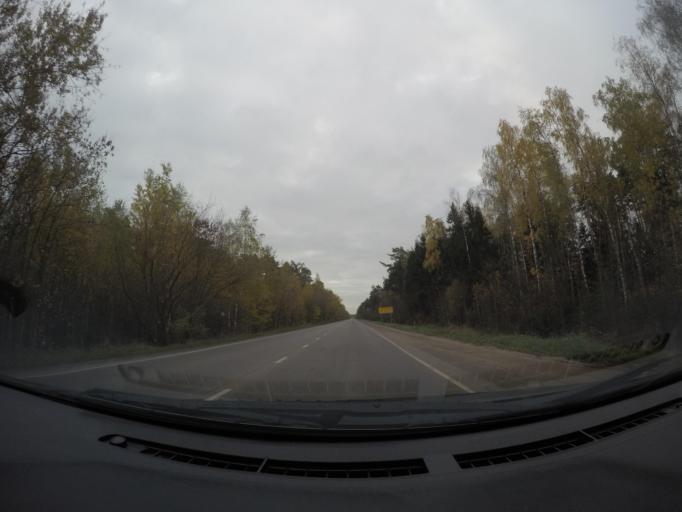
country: RU
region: Moskovskaya
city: Obukhovo
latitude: 55.7798
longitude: 38.2503
